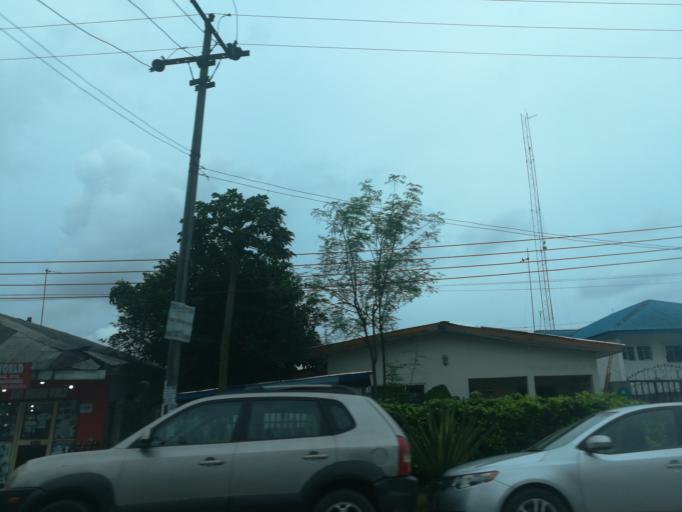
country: NG
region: Rivers
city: Port Harcourt
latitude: 4.8138
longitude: 7.0019
